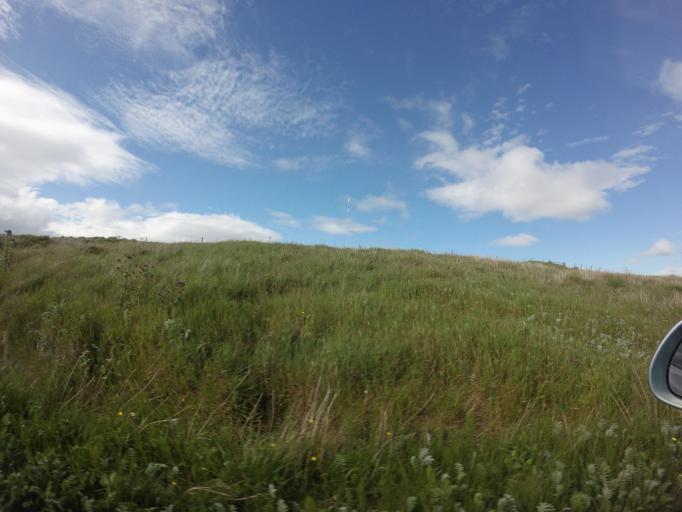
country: GB
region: Scotland
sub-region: Eilean Siar
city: Stornoway
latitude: 58.1723
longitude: -6.5880
